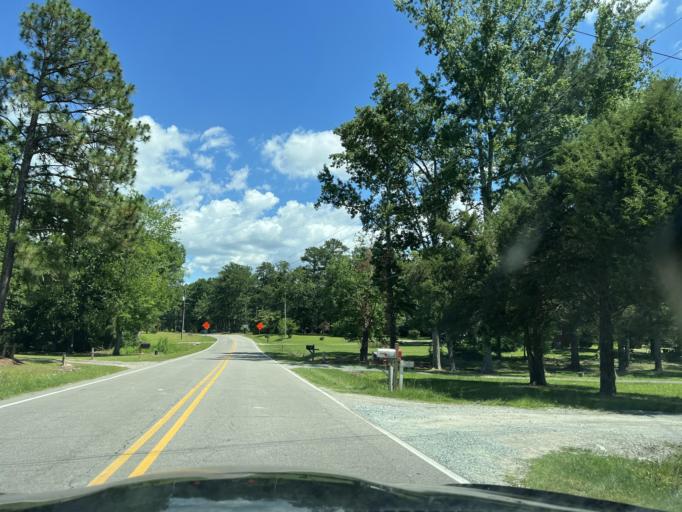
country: US
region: North Carolina
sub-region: Lee County
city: Sanford
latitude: 35.4398
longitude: -79.1728
